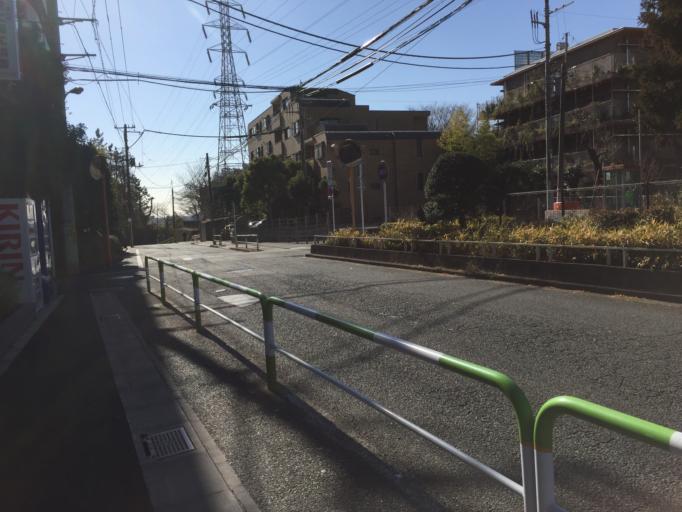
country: JP
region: Tokyo
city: Chofugaoka
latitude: 35.6352
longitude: 139.6001
